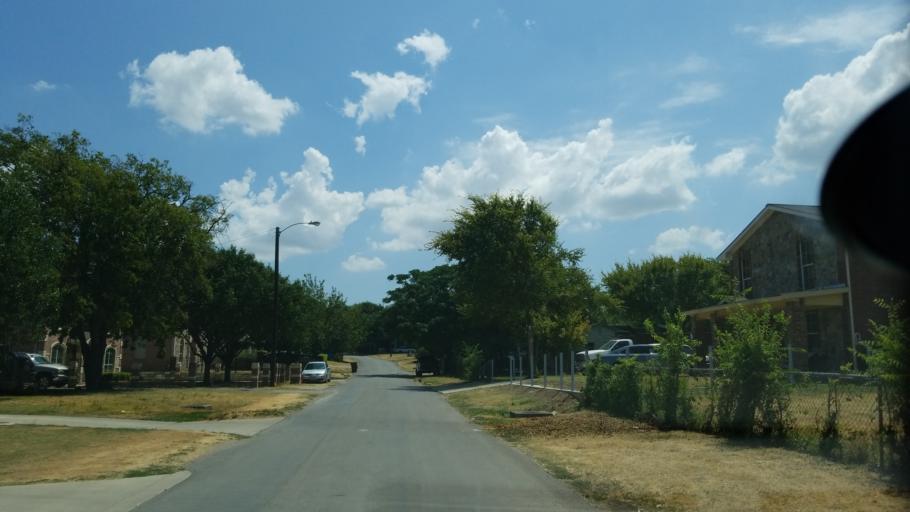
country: US
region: Texas
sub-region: Dallas County
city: Cockrell Hill
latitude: 32.7312
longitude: -96.8945
